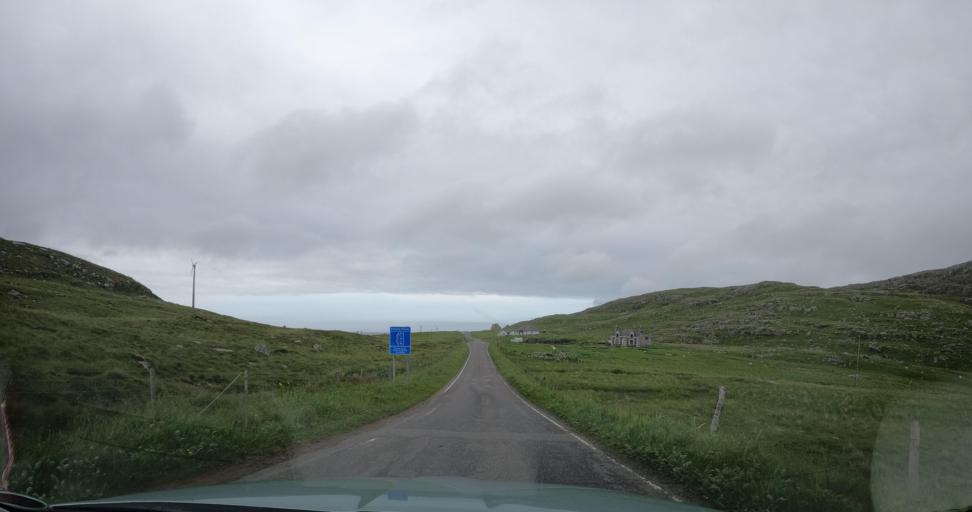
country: GB
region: Scotland
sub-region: Eilean Siar
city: Barra
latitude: 56.9631
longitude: -7.5092
